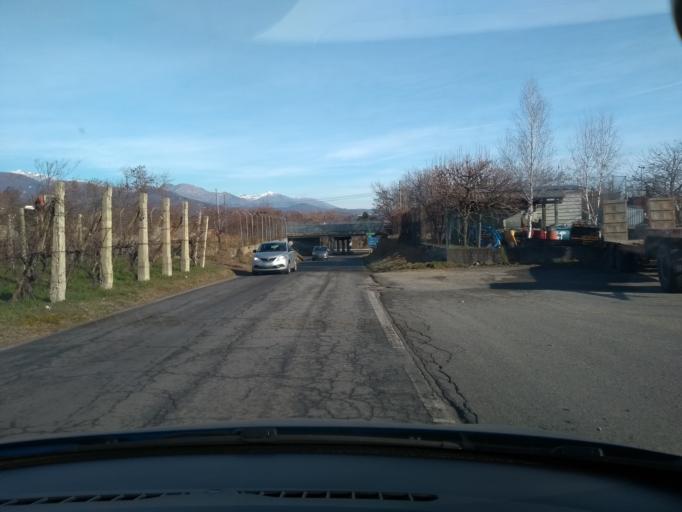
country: IT
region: Piedmont
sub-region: Provincia di Torino
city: Valperga
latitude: 45.3740
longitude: 7.6679
